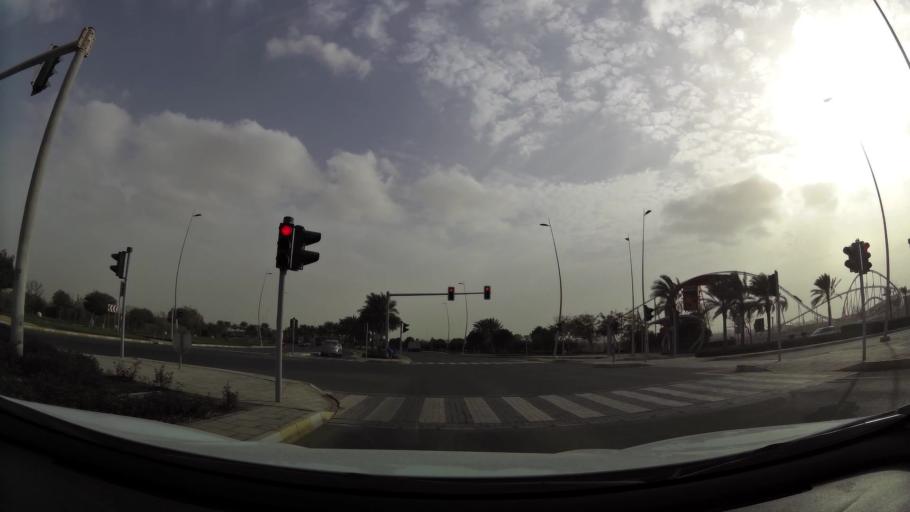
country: AE
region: Abu Dhabi
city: Abu Dhabi
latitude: 24.4859
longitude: 54.6151
